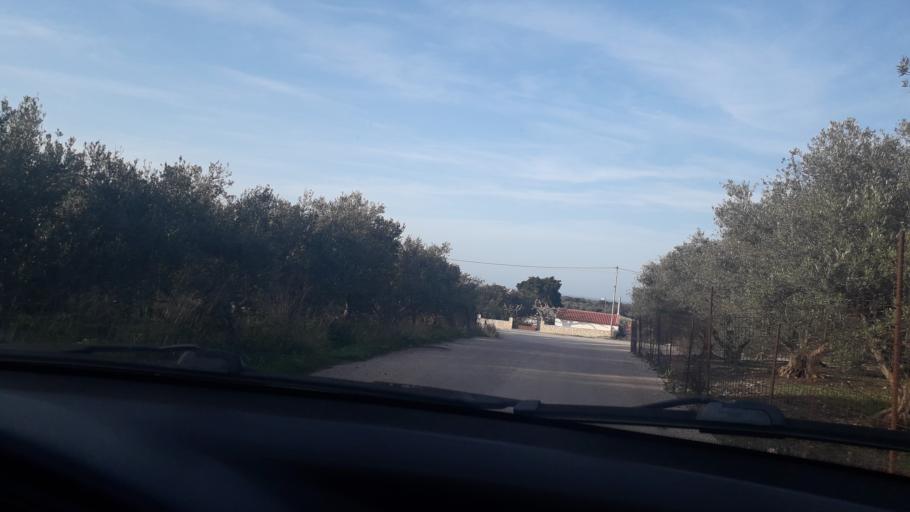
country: GR
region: Crete
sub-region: Nomos Rethymnis
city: Panormos
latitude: 35.3868
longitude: 24.6242
